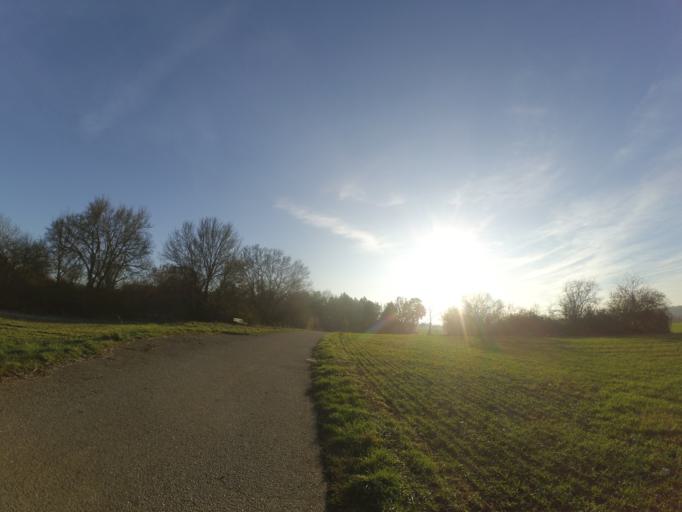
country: DE
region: Baden-Wuerttemberg
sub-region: Tuebingen Region
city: Dornstadt
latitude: 48.4405
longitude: 9.8970
